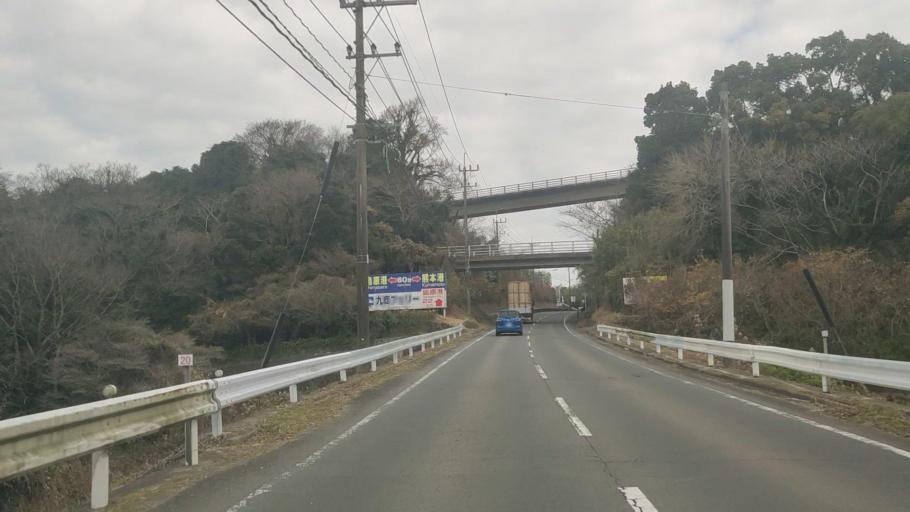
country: JP
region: Nagasaki
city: Shimabara
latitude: 32.8509
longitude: 130.2398
